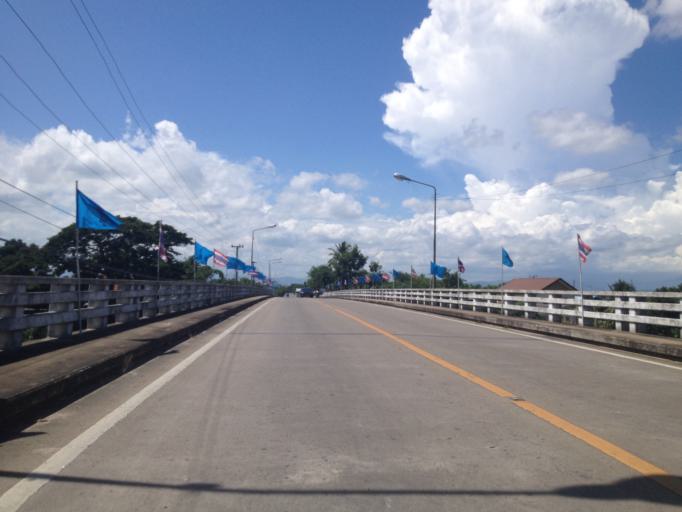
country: TH
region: Lamphun
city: Lamphun
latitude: 18.5987
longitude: 98.9666
